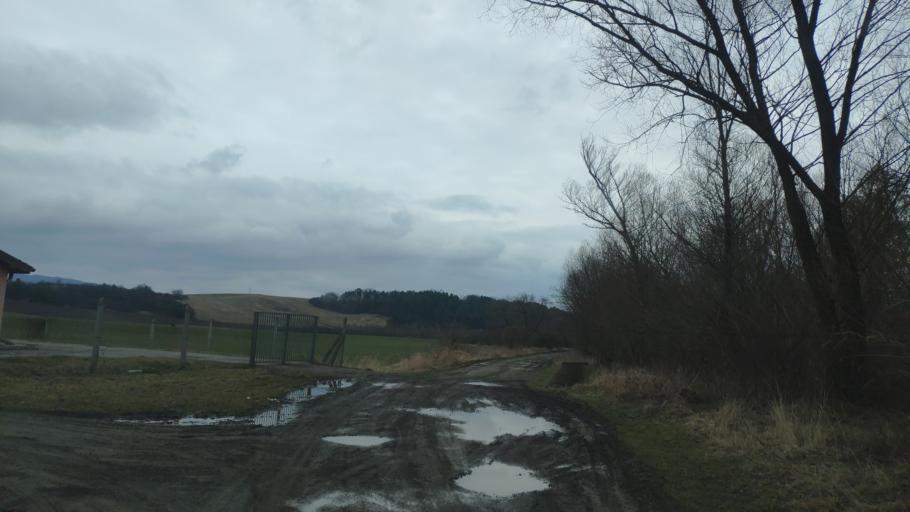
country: SK
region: Presovsky
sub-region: Okres Presov
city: Presov
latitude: 49.0895
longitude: 21.2768
